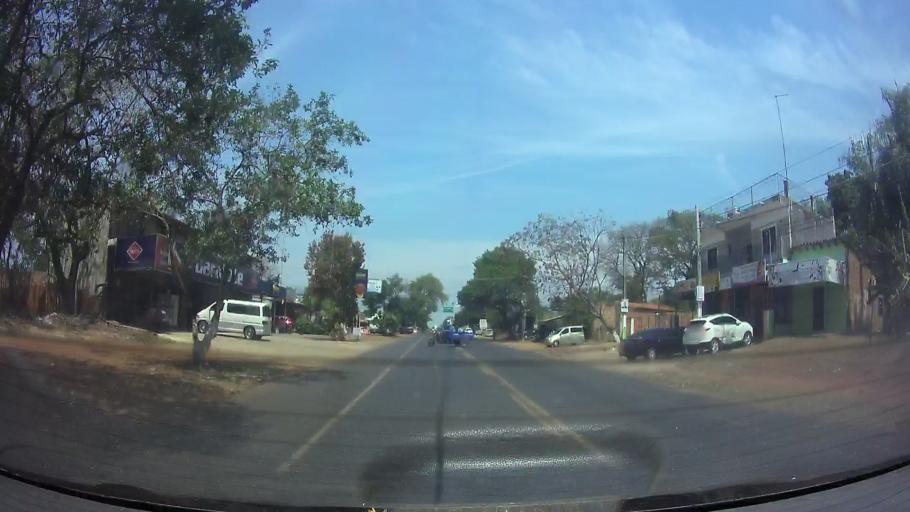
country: PY
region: Central
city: Guarambare
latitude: -25.4440
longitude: -57.4405
